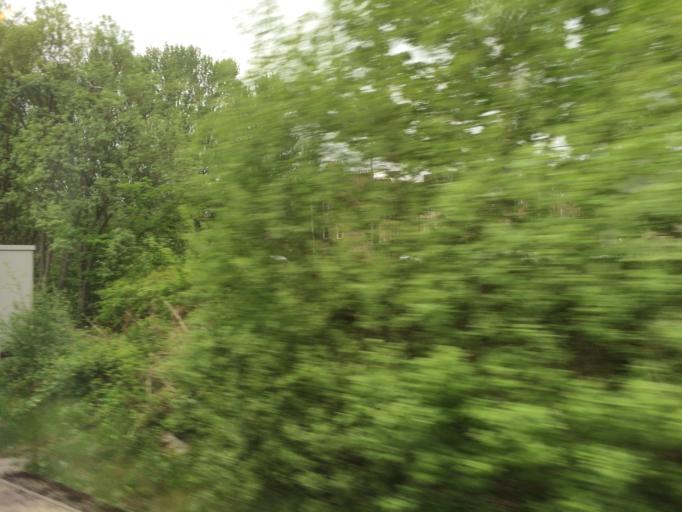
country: GB
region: Scotland
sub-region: Stirling
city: Stirling
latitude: 56.1232
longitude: -3.9366
